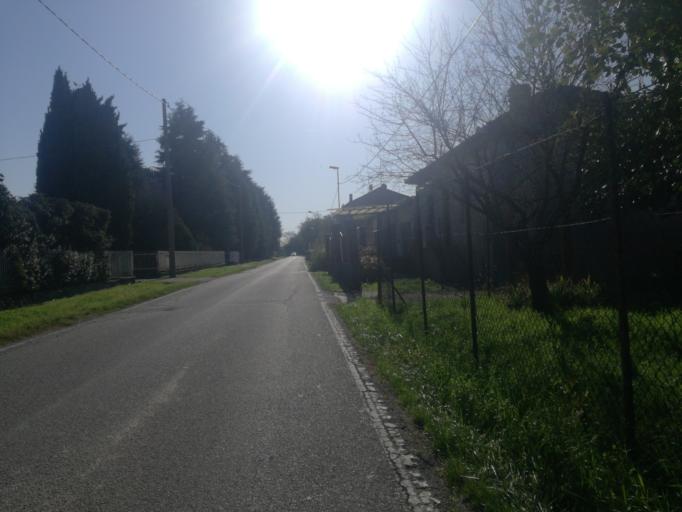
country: IT
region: Lombardy
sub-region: Provincia di Monza e Brianza
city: Porto d'Adda
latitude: 45.6476
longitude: 9.4777
